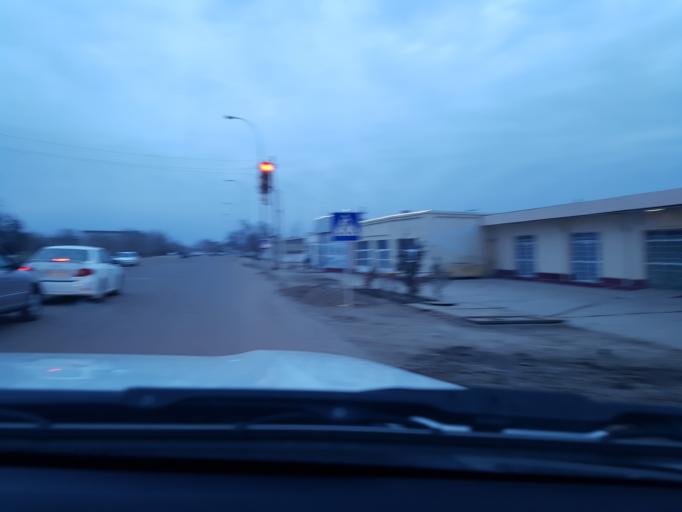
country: TM
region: Dasoguz
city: Yylanly
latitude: 41.8800
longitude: 59.6283
